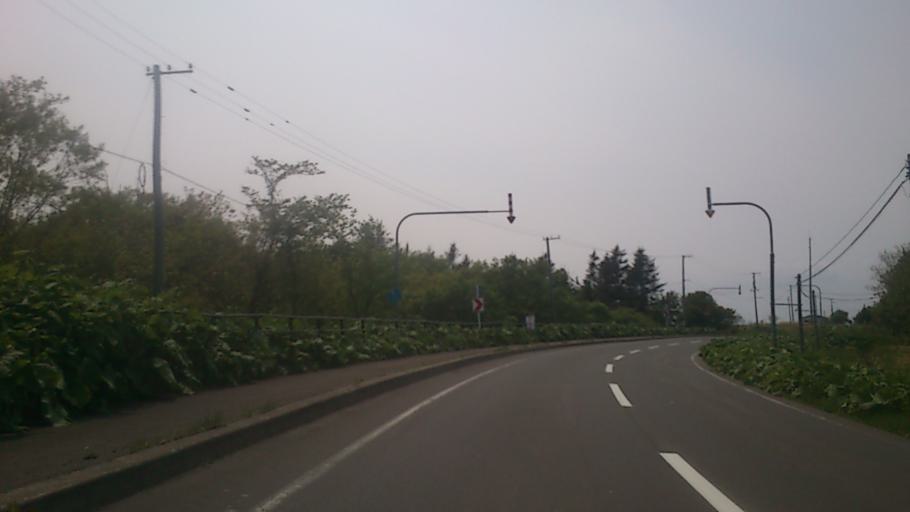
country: JP
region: Hokkaido
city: Nemuro
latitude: 43.2785
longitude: 145.5128
